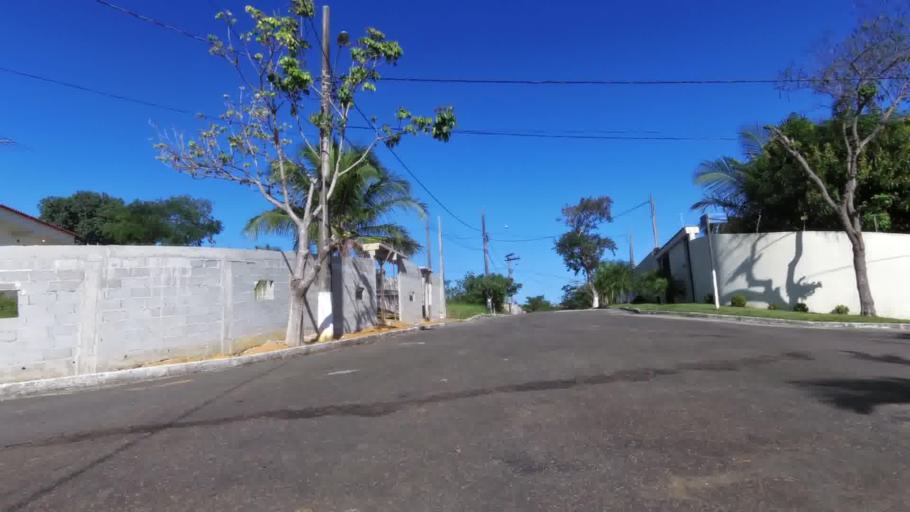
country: BR
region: Espirito Santo
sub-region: Guarapari
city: Guarapari
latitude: -20.7400
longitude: -40.5590
